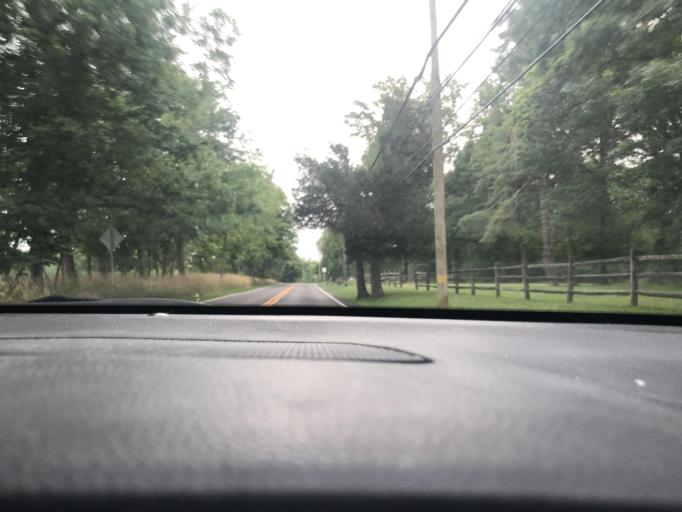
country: US
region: Pennsylvania
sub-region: Montgomery County
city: Blue Bell
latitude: 40.1659
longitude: -75.2550
